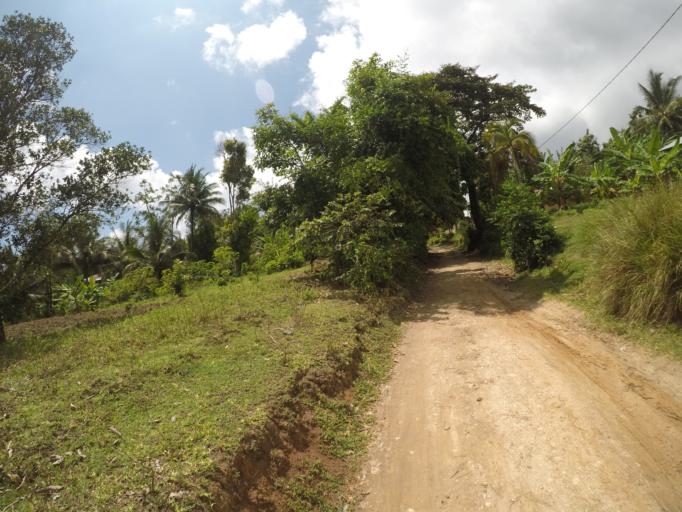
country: TZ
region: Pemba South
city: Mtambile
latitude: -5.3910
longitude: 39.7384
